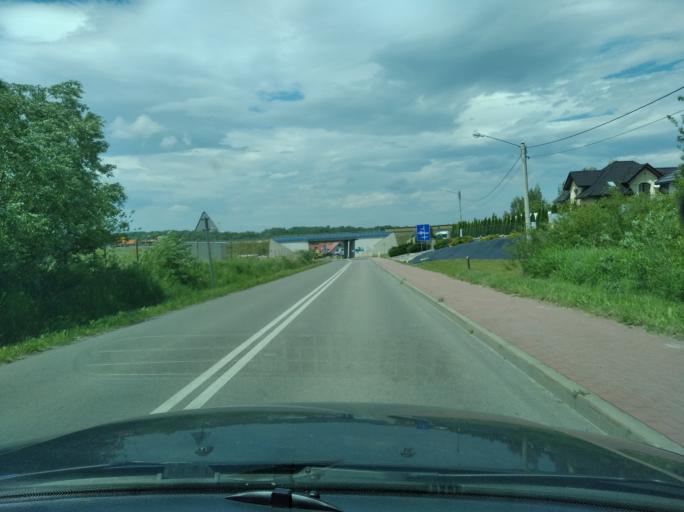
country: PL
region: Subcarpathian Voivodeship
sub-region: Powiat ropczycko-sedziszowski
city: Ropczyce
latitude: 50.0488
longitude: 21.6219
